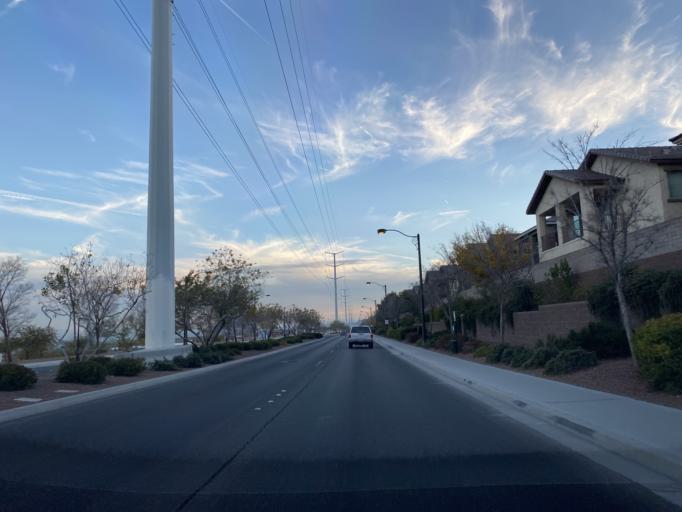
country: US
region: Nevada
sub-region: Clark County
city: Summerlin South
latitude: 36.2860
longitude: -115.3289
